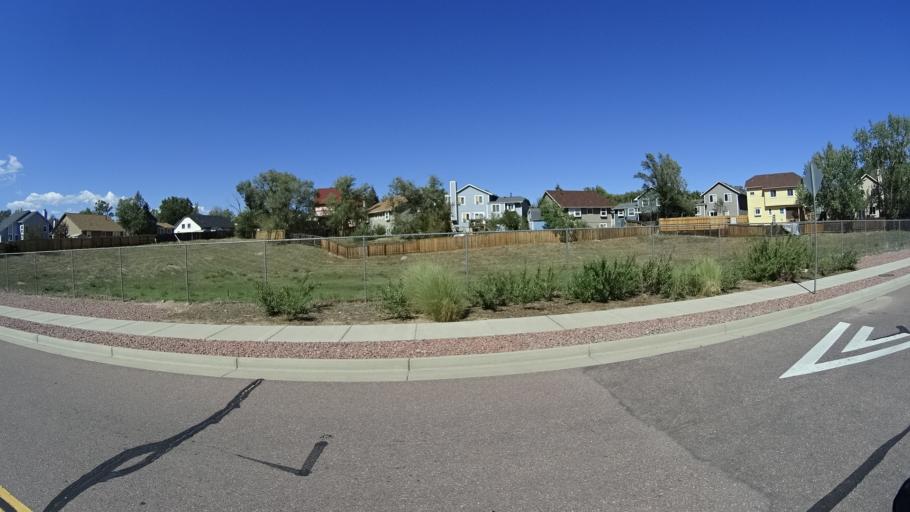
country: US
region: Colorado
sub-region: El Paso County
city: Stratmoor
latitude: 38.7817
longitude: -104.7454
